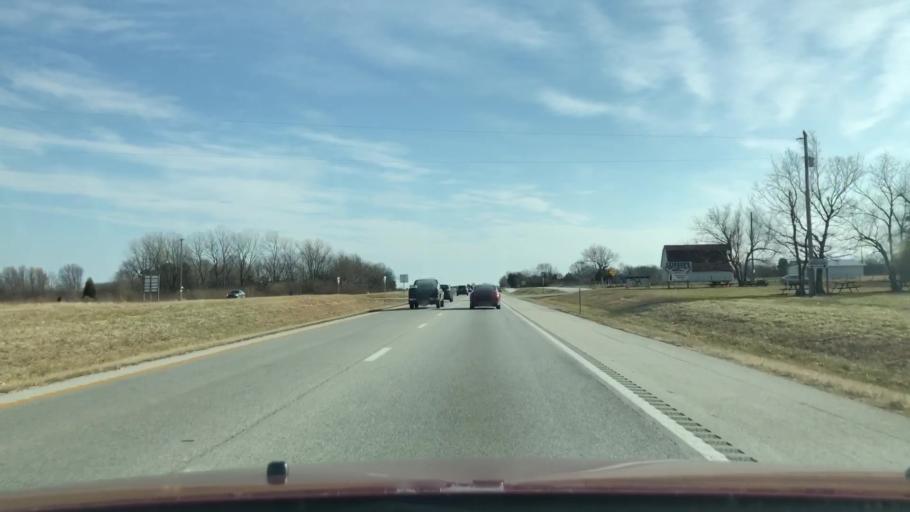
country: US
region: Missouri
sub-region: Webster County
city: Rogersville
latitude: 37.1182
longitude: -93.1024
